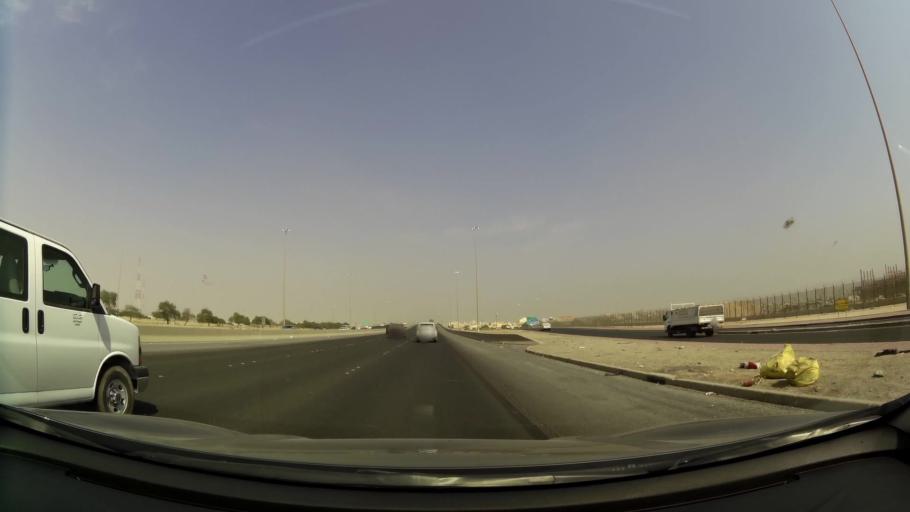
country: KW
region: Al Ahmadi
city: Al Fahahil
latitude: 29.0681
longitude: 48.1105
